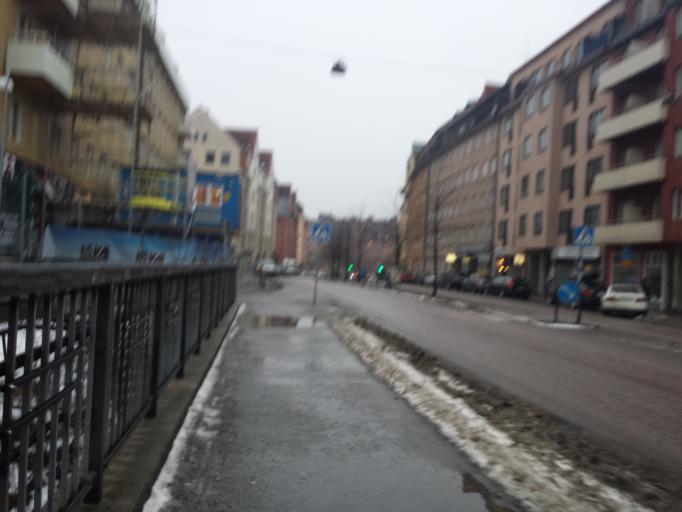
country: SE
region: Stockholm
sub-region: Solna Kommun
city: Solna
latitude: 59.3655
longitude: 17.9984
